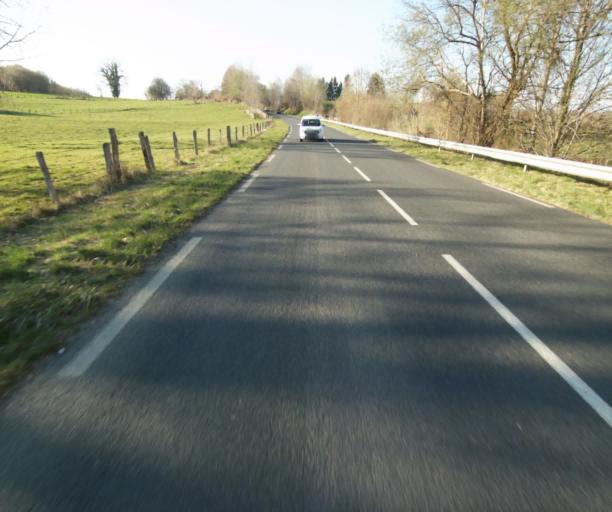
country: FR
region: Limousin
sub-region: Departement de la Correze
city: Chamboulive
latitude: 45.4069
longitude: 1.7198
